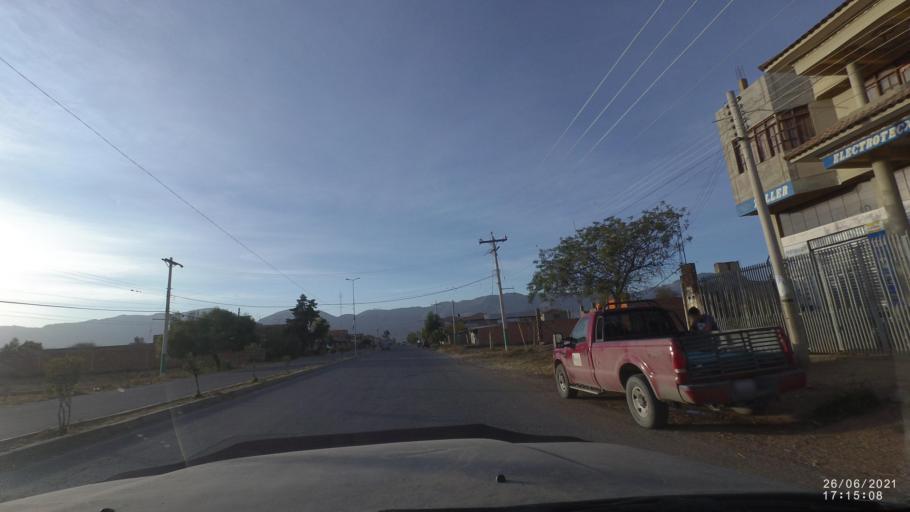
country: BO
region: Cochabamba
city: Cliza
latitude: -17.5774
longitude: -65.9341
